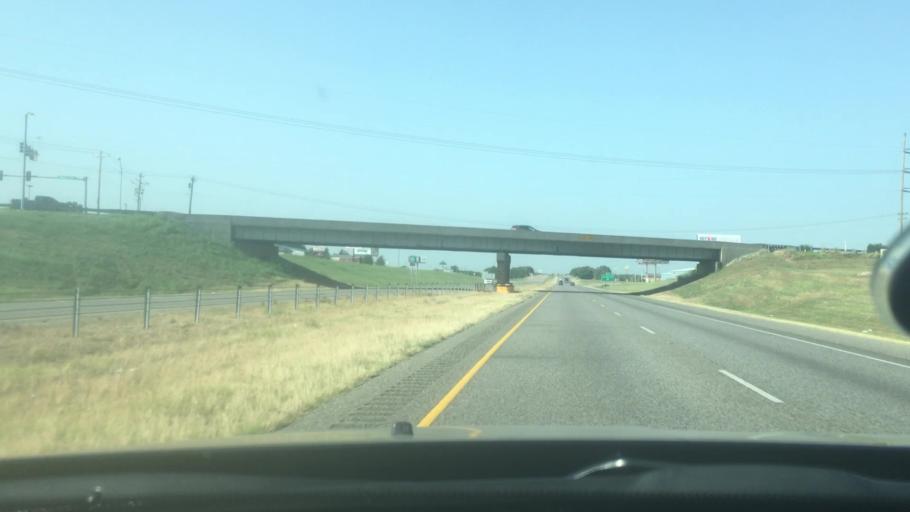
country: US
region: Oklahoma
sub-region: Bryan County
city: Durant
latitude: 34.0059
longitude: -96.3992
